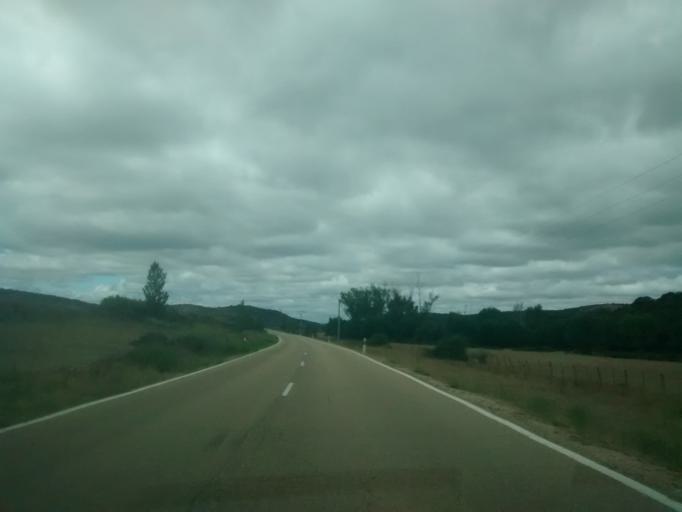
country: ES
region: Castille and Leon
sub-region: Provincia de Salamanca
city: Ciudad Rodrigo
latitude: 40.6465
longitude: -6.4661
